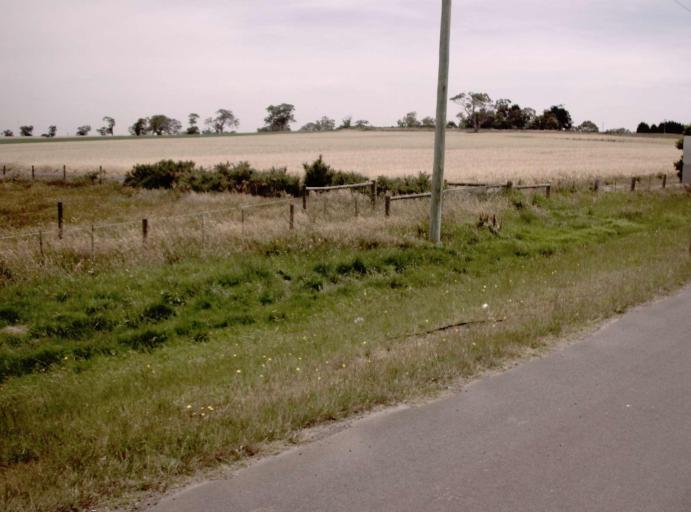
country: AU
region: Victoria
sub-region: Casey
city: Lynbrook
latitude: -38.0705
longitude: 145.2407
